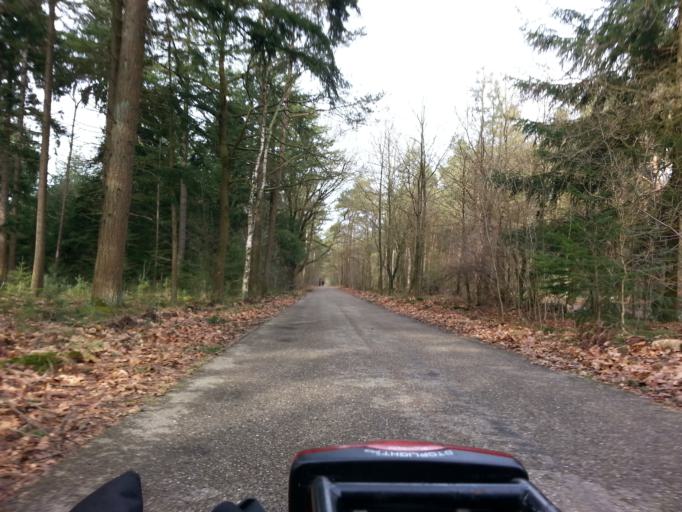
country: NL
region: Utrecht
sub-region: Gemeente Utrechtse Heuvelrug
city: Driebergen-Rijsenburg
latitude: 52.1042
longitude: 5.3184
